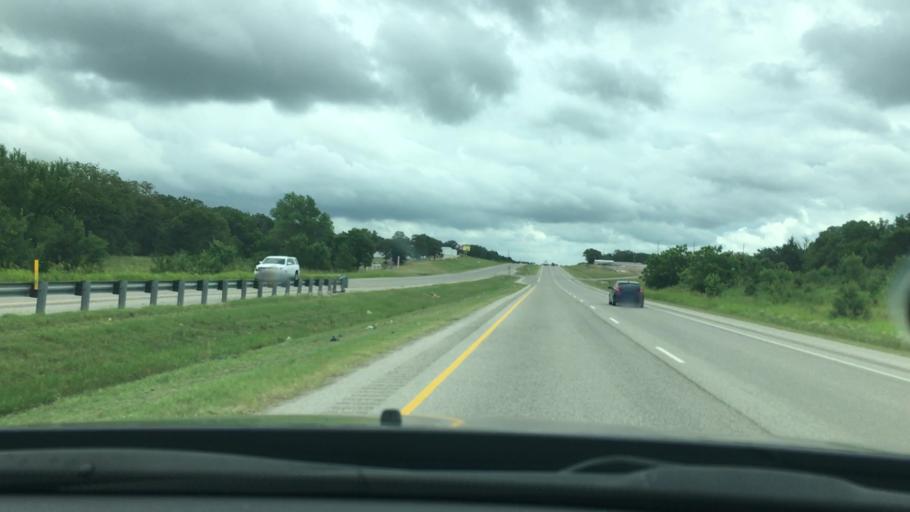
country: US
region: Oklahoma
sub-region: Carter County
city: Ardmore
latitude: 34.1345
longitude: -97.1020
